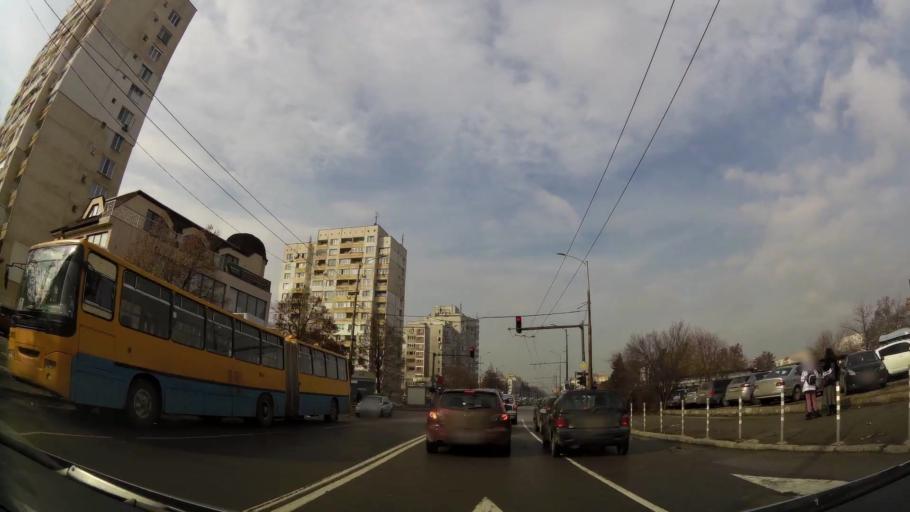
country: BG
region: Sofiya
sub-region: Obshtina Bozhurishte
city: Bozhurishte
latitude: 42.7146
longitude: 23.2537
